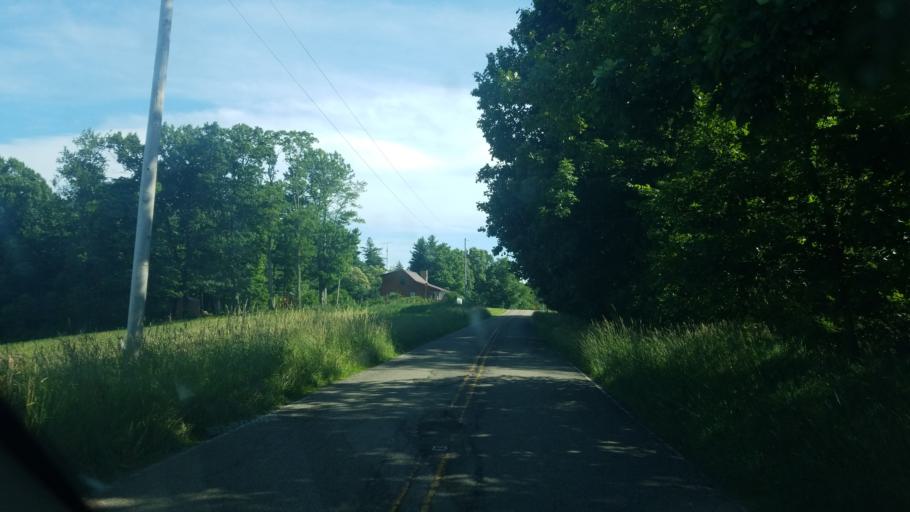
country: US
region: Ohio
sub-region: Holmes County
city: Millersburg
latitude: 40.4375
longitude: -81.9512
